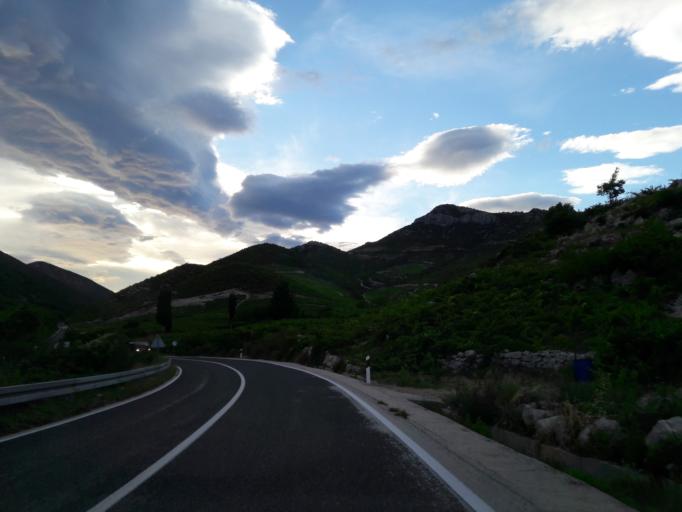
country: HR
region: Dubrovacko-Neretvanska
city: Ston
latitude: 42.8250
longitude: 17.6690
